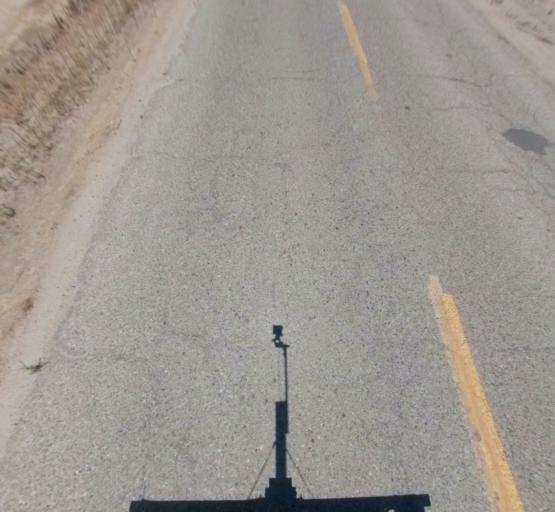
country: US
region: California
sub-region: Madera County
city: Parkwood
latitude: 36.8792
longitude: -120.1104
